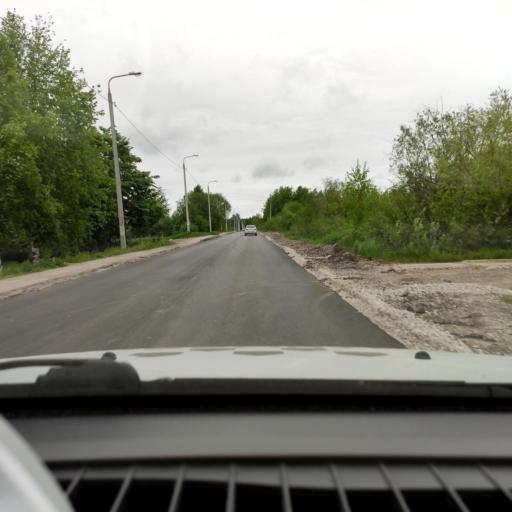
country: RU
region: Perm
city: Novyye Lyady
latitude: 58.0475
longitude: 56.6076
